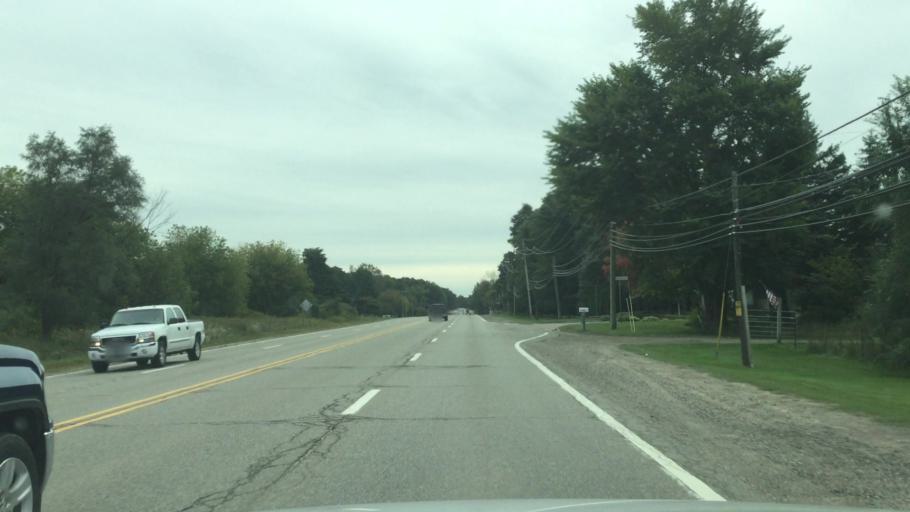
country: US
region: Michigan
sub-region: Oakland County
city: Clarkston
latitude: 42.7729
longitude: -83.4920
